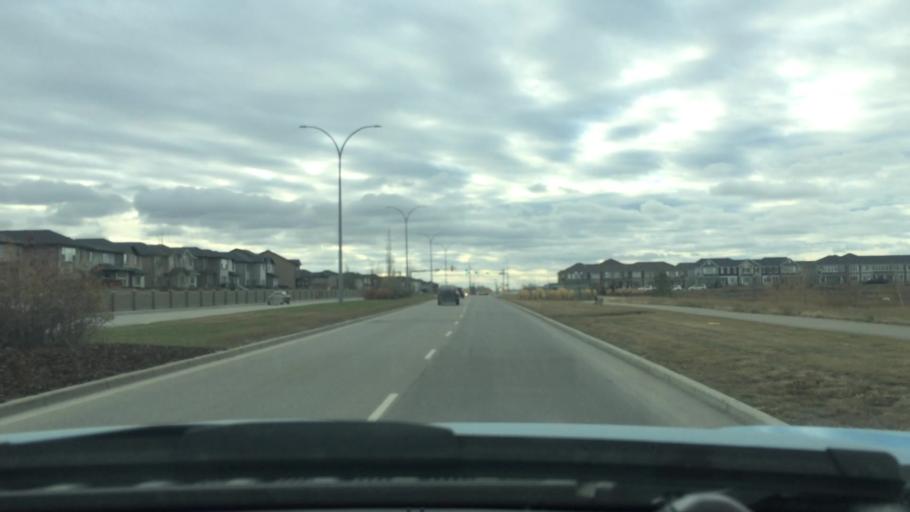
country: CA
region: Alberta
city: Airdrie
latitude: 51.2553
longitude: -114.0252
